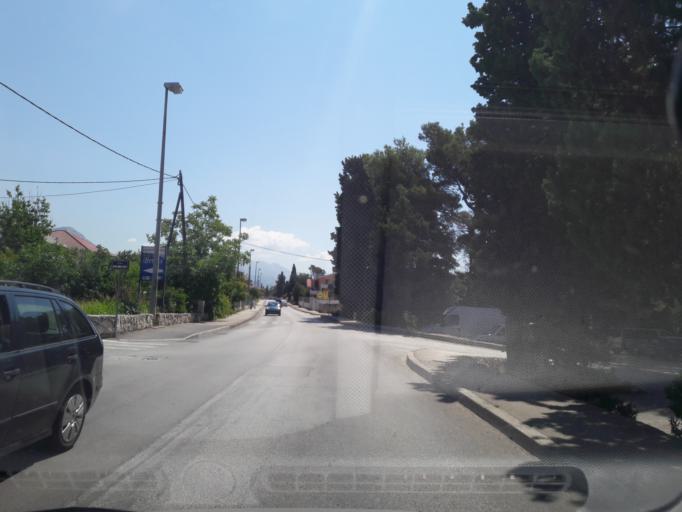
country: HR
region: Splitsko-Dalmatinska
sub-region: Grad Split
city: Split
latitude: 43.5475
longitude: 16.4040
